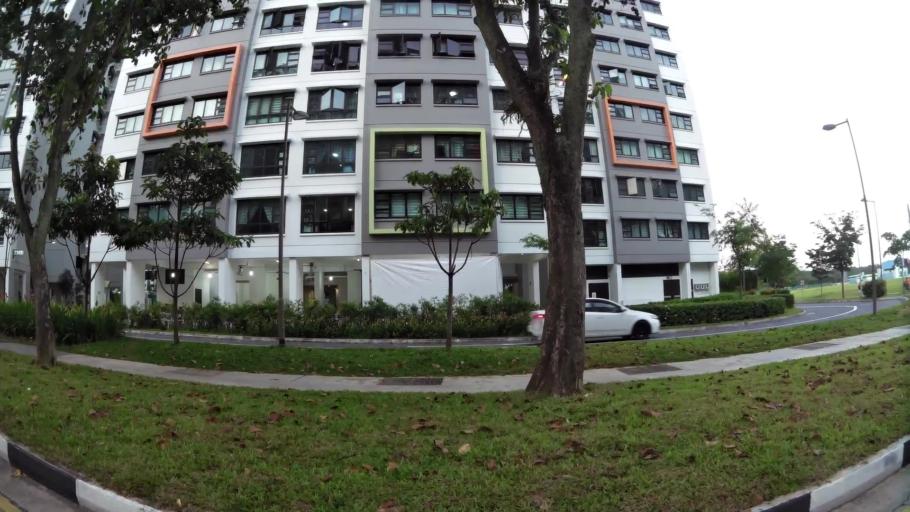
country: MY
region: Johor
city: Kampung Pasir Gudang Baru
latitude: 1.4310
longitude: 103.8446
